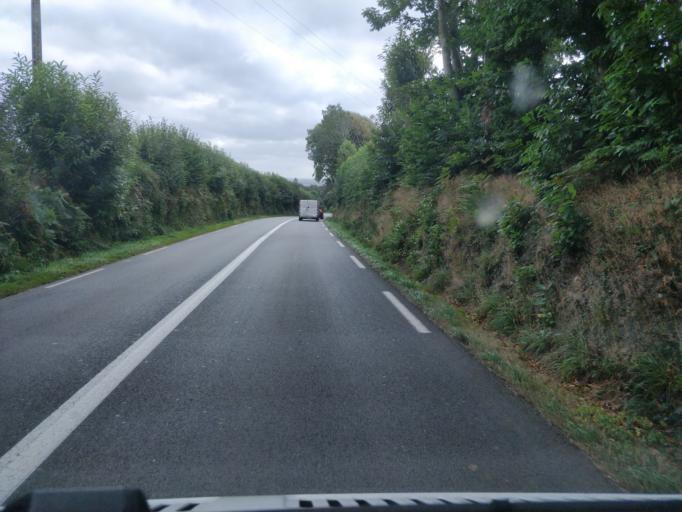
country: FR
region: Brittany
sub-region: Departement du Finistere
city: Pluguffan
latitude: 48.0002
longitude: -4.1703
